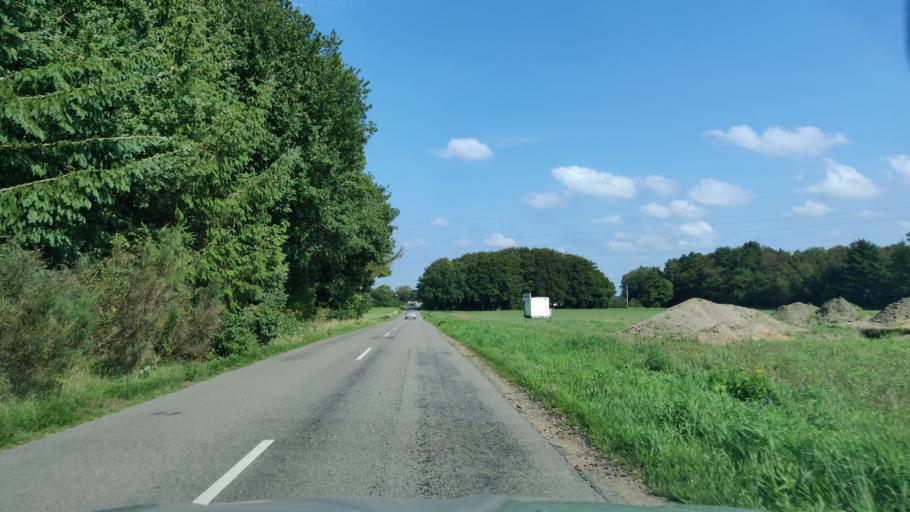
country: DK
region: Central Jutland
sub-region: Herning Kommune
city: Avlum
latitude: 56.2296
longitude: 8.8657
